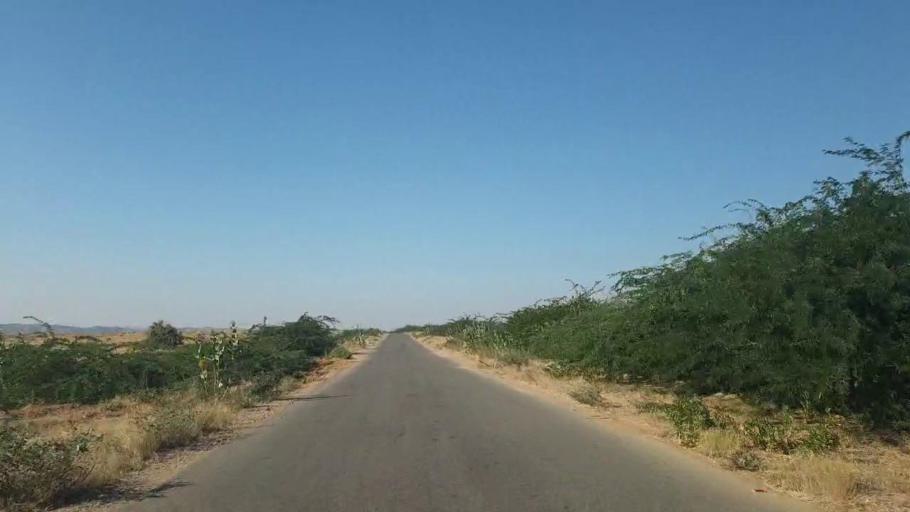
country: PK
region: Sindh
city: Malir Cantonment
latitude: 25.2686
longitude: 67.5944
